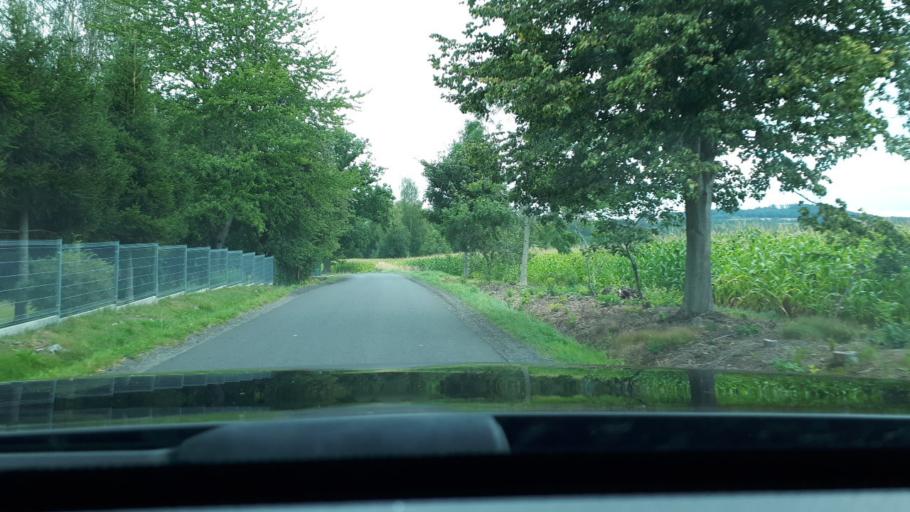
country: PL
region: Lower Silesian Voivodeship
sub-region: Powiat lubanski
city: Lesna
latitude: 51.0363
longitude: 15.3113
